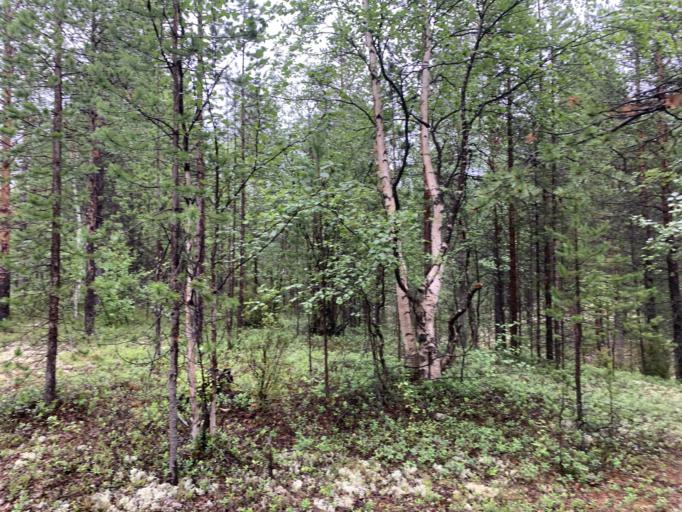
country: RU
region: Murmansk
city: Monchegorsk
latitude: 67.9493
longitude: 33.0248
